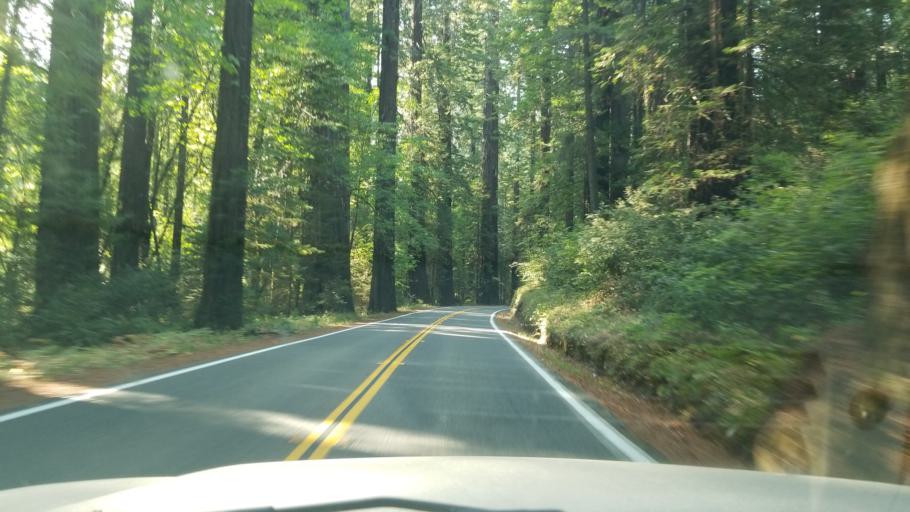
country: US
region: California
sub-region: Humboldt County
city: Redway
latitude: 40.2600
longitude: -123.8421
